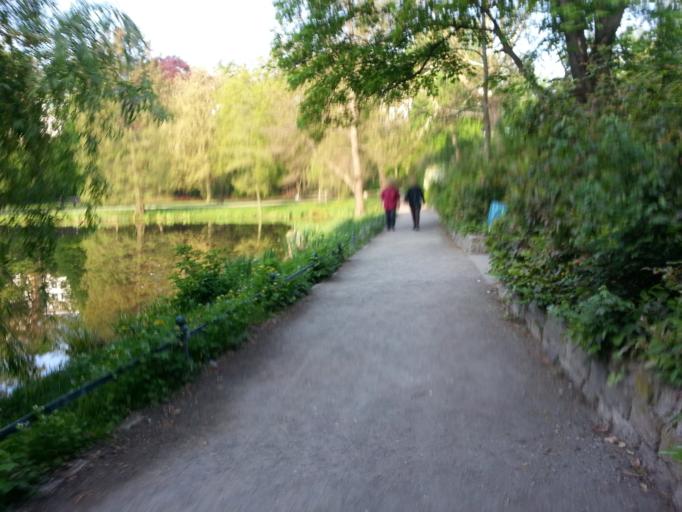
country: DE
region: Berlin
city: Charlottenburg Bezirk
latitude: 52.5063
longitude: 13.2877
